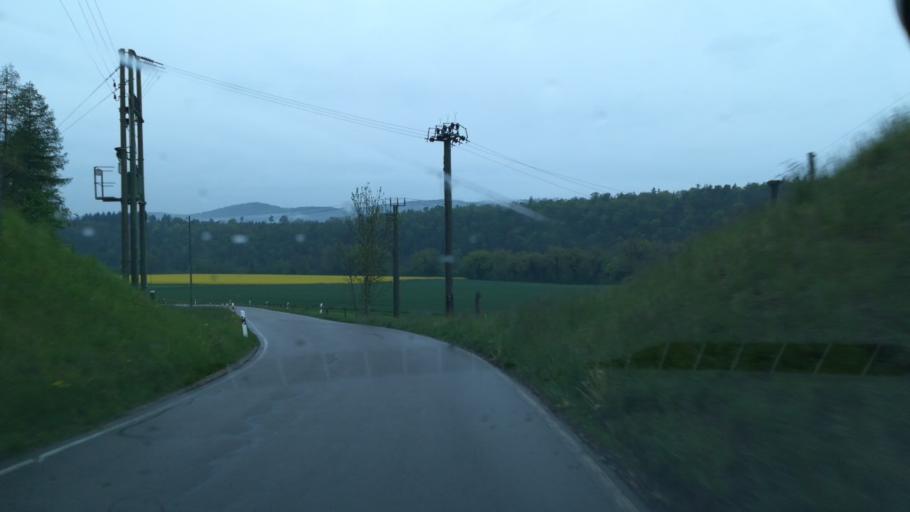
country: CH
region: Zurich
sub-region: Bezirk Buelach
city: Glattfelden
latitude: 47.5776
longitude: 8.5018
